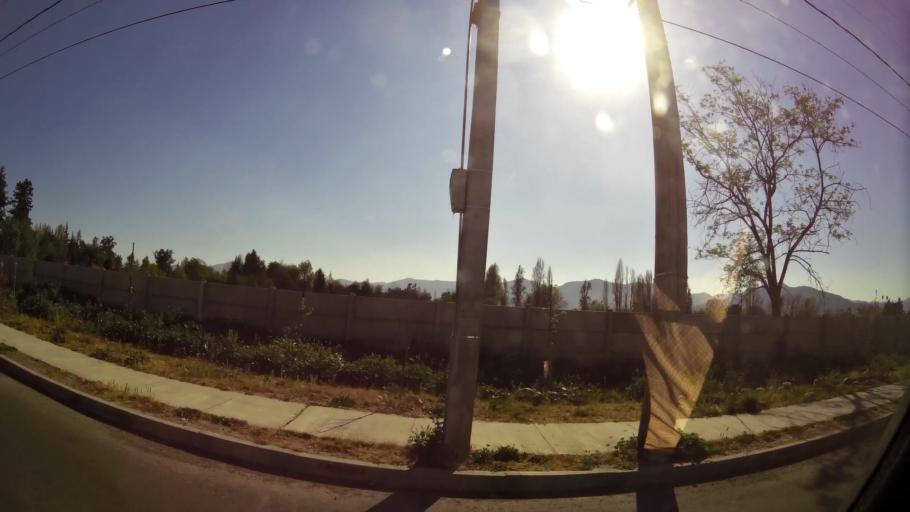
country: CL
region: Santiago Metropolitan
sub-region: Provincia de Talagante
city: Penaflor
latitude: -33.6149
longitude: -70.8810
